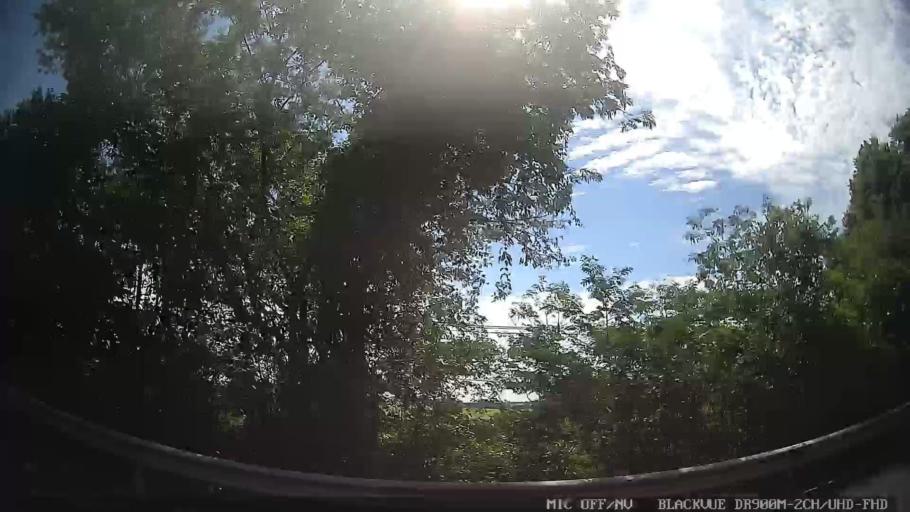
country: BR
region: Sao Paulo
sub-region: Porto Feliz
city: Porto Feliz
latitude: -23.2213
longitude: -47.5723
